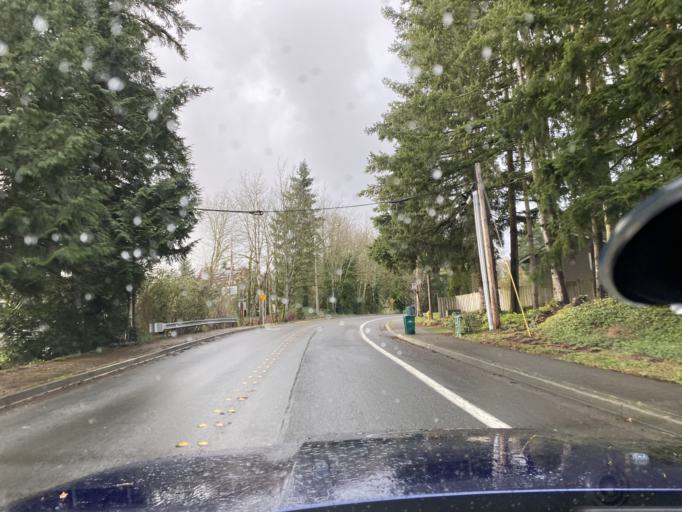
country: US
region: Washington
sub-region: King County
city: Redmond
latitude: 47.6551
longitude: -122.1266
